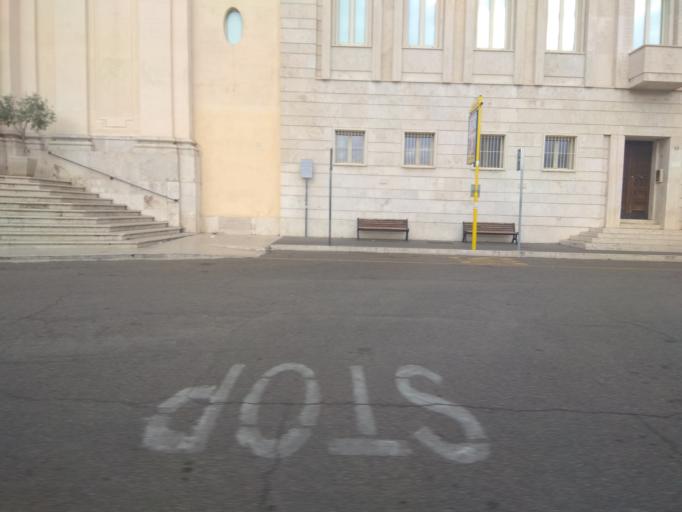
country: IT
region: Latium
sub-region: Citta metropolitana di Roma Capitale
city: Civitavecchia
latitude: 42.0922
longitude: 11.7920
